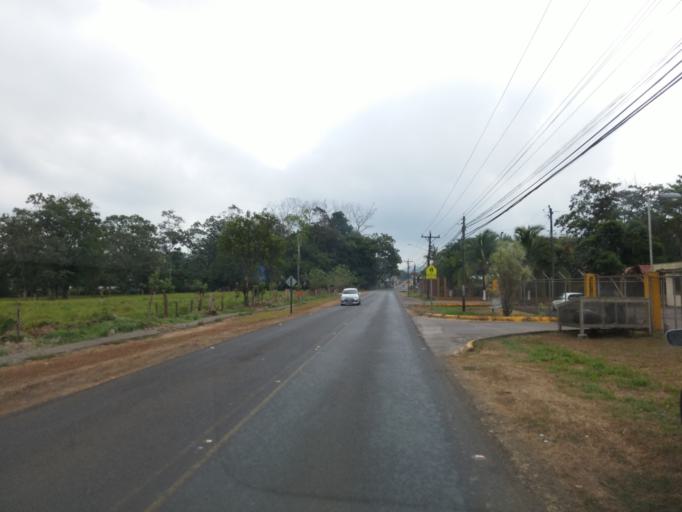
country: CR
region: Alajuela
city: Quesada
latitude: 10.3588
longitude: -84.5111
